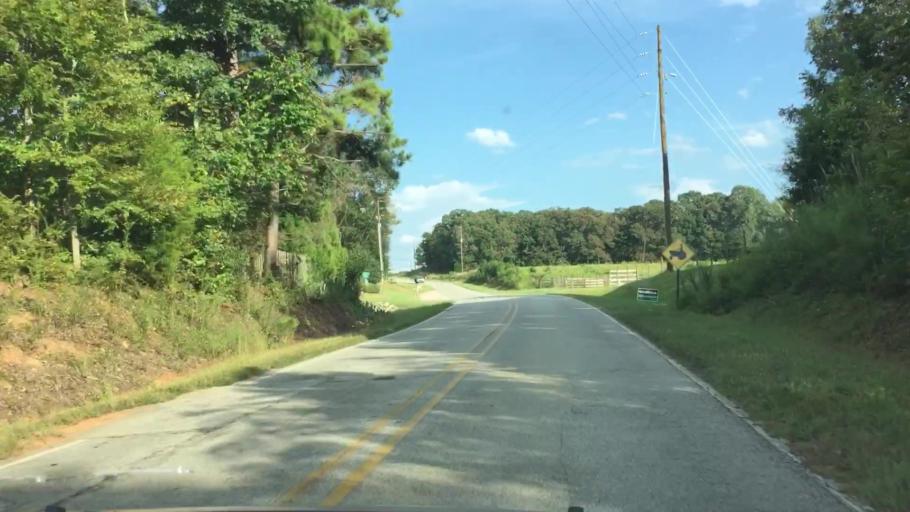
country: US
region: Georgia
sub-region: Newton County
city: Oakwood
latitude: 33.4752
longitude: -84.0254
